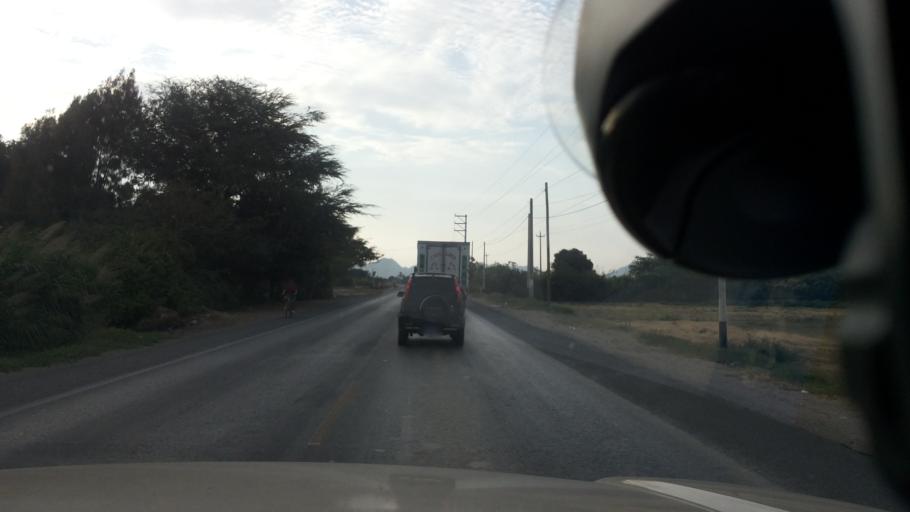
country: PE
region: Ancash
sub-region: Provincia de Casma
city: Casma
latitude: -9.4550
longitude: -78.3383
